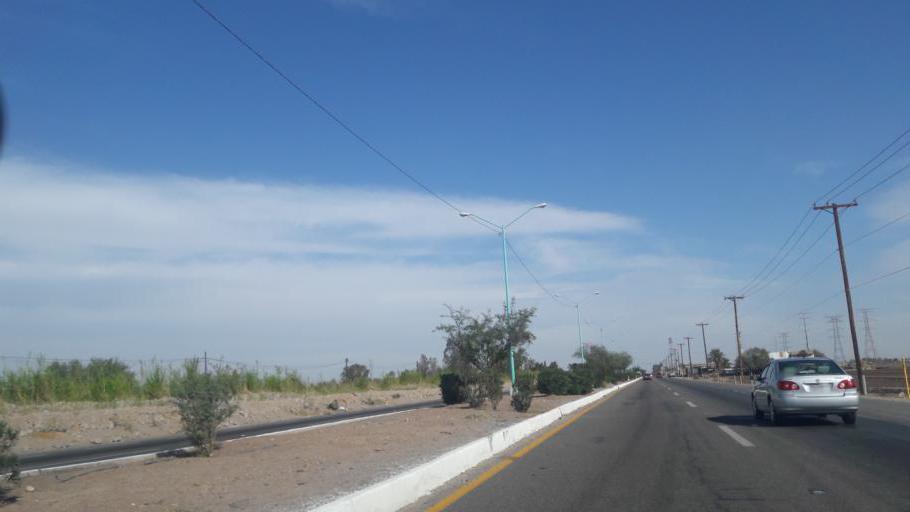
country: MX
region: Baja California
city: Progreso
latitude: 32.5880
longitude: -115.5647
